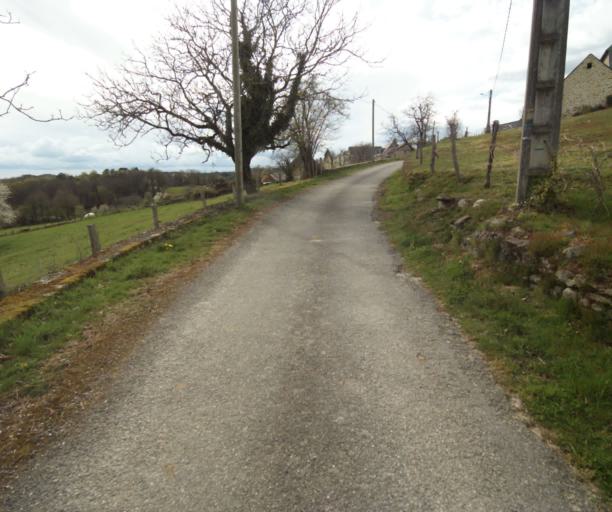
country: FR
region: Limousin
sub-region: Departement de la Correze
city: Argentat
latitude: 45.1789
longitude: 1.9451
